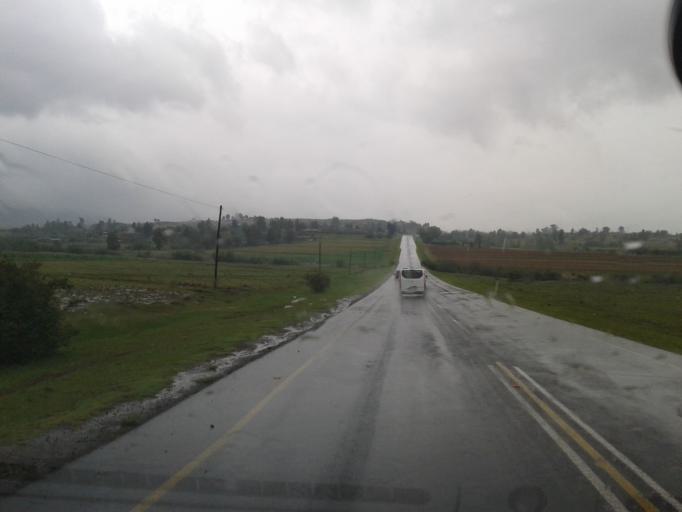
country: LS
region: Maseru
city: Nako
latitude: -29.6354
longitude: 27.4797
